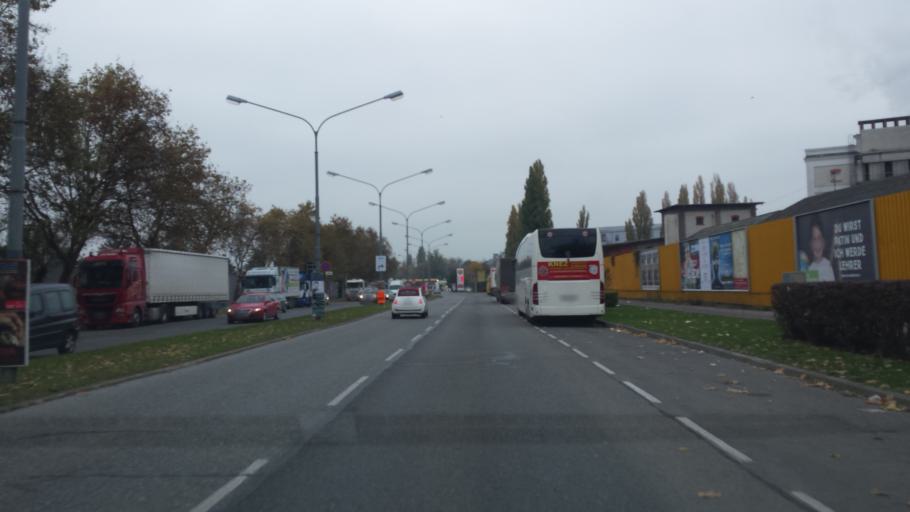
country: AT
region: Vienna
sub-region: Wien Stadt
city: Vienna
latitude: 48.2238
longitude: 16.4445
